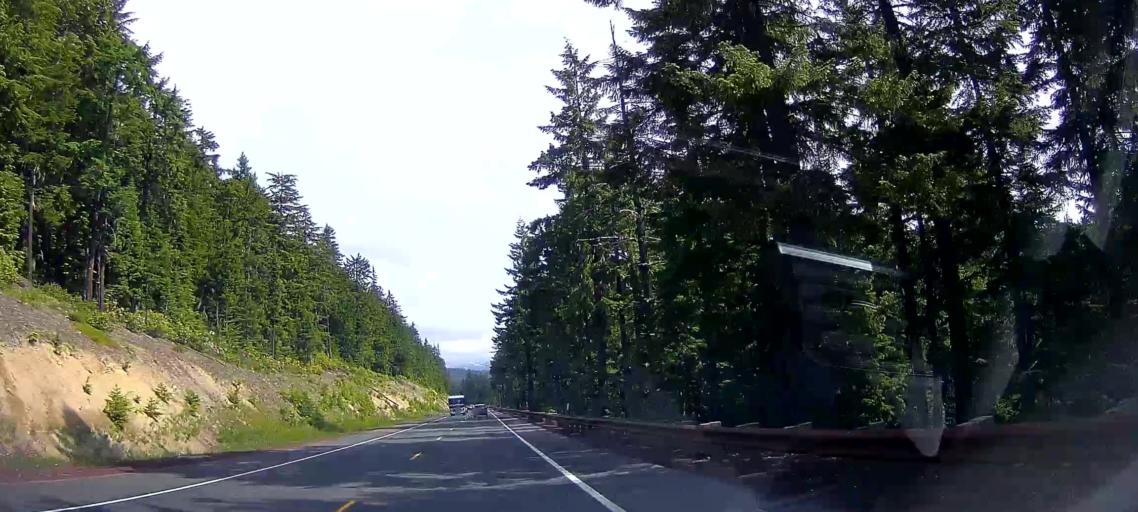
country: US
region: Oregon
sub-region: Clackamas County
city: Mount Hood Village
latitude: 45.2127
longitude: -121.6987
